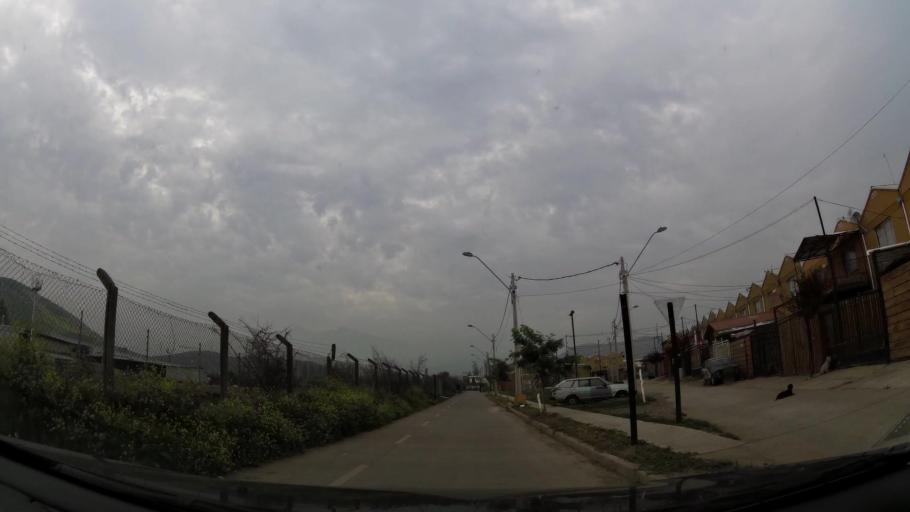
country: CL
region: Santiago Metropolitan
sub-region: Provincia de Chacabuco
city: Chicureo Abajo
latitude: -33.1829
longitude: -70.6664
